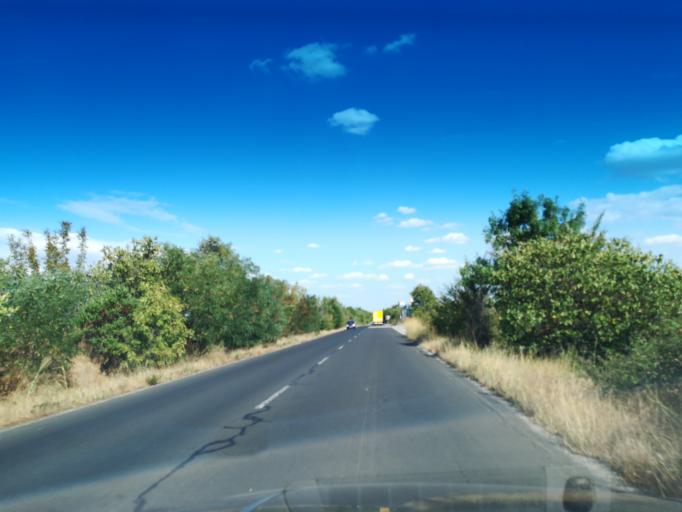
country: BG
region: Khaskovo
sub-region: Obshtina Mineralni Bani
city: Mineralni Bani
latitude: 42.0553
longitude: 25.3045
